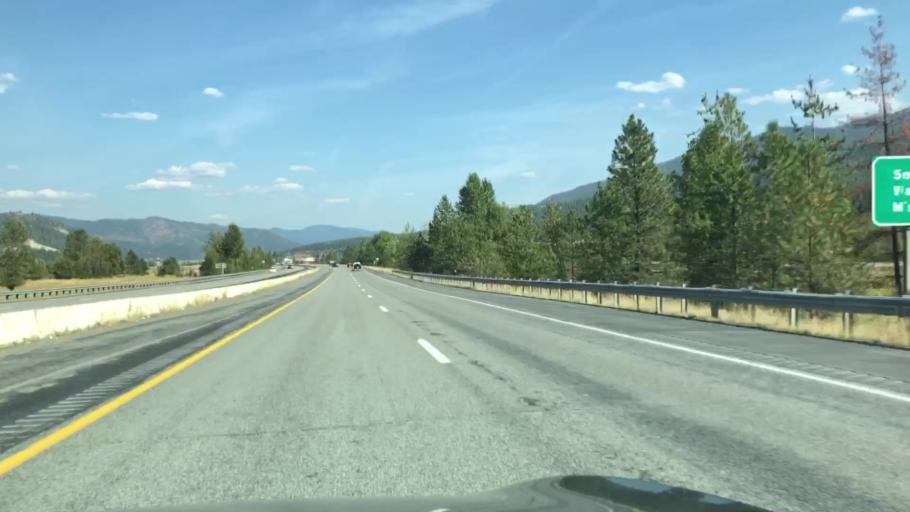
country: US
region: Idaho
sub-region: Shoshone County
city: Pinehurst
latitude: 47.5472
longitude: -116.2154
